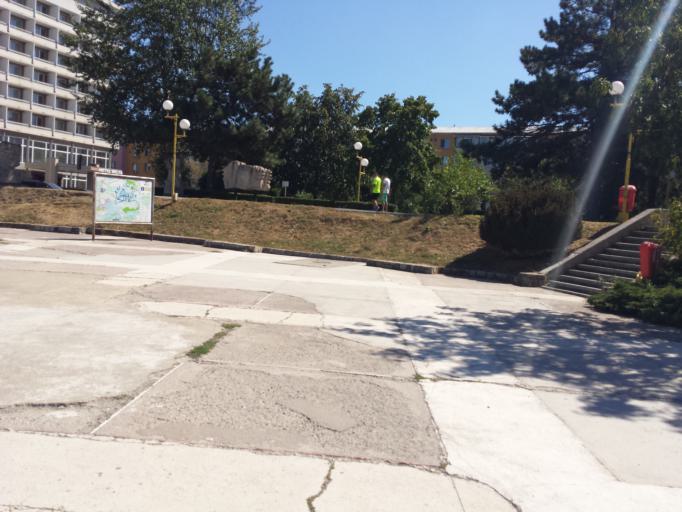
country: RO
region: Tulcea
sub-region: Municipiul Tulcea
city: Tulcea
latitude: 45.1798
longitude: 28.8025
